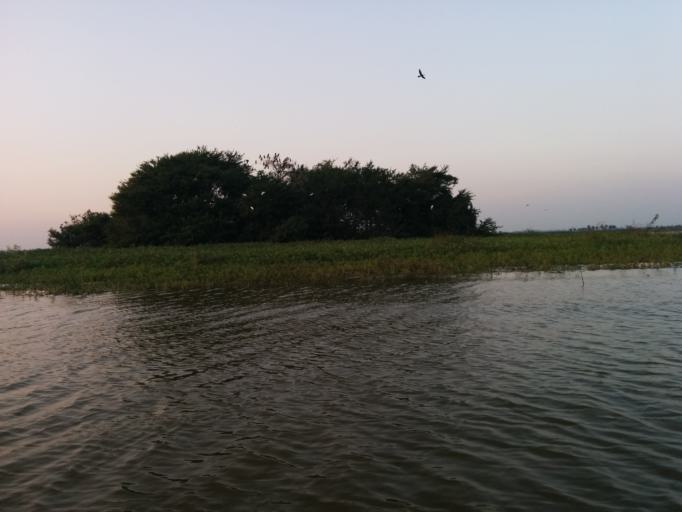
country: IN
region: Tamil Nadu
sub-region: Villupuram
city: Auroville
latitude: 11.9555
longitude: 79.7489
